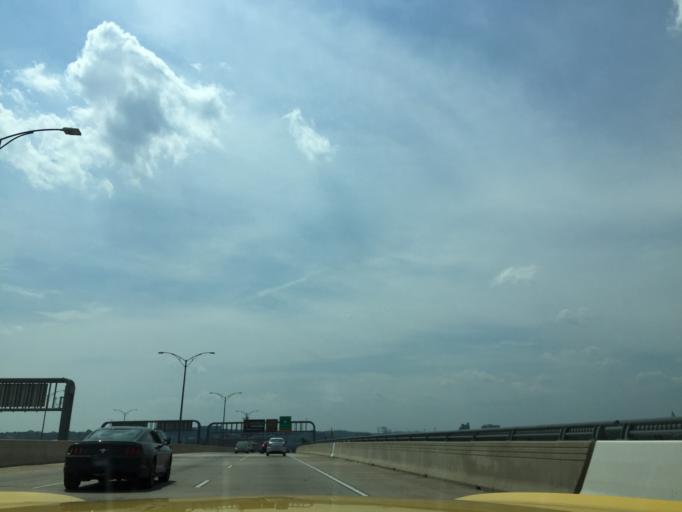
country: US
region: Virginia
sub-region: City of Alexandria
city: Alexandria
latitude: 38.7930
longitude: -77.0377
